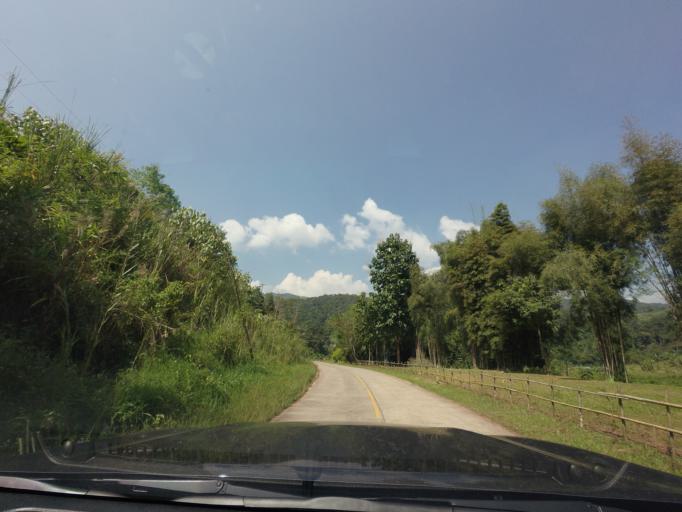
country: TH
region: Nan
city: Bo Kluea
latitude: 19.1975
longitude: 101.1871
